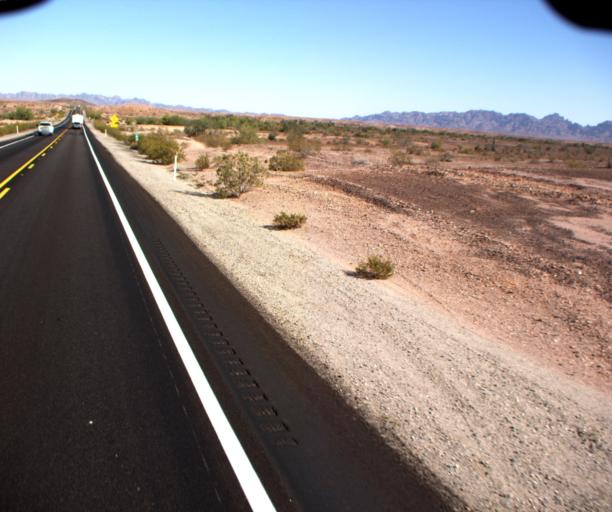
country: US
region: Arizona
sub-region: Yuma County
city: Wellton
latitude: 33.0764
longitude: -114.2950
